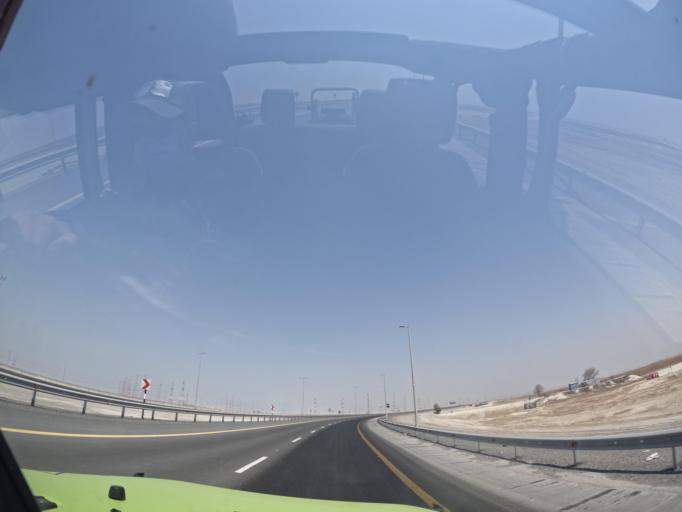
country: AE
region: Abu Dhabi
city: Abu Dhabi
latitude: 24.1496
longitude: 54.2428
